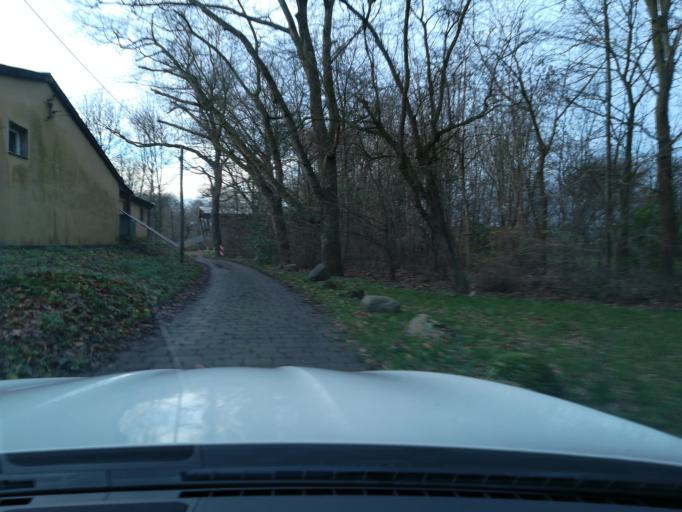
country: DE
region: Hamburg
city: Harburg
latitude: 53.4703
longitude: 10.0041
